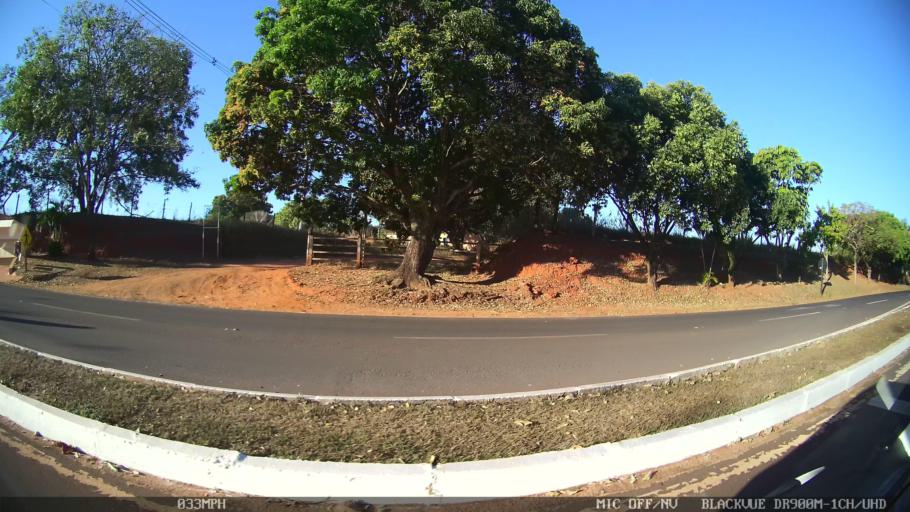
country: BR
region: Sao Paulo
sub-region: Guapiacu
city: Guapiacu
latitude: -20.7900
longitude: -49.2225
